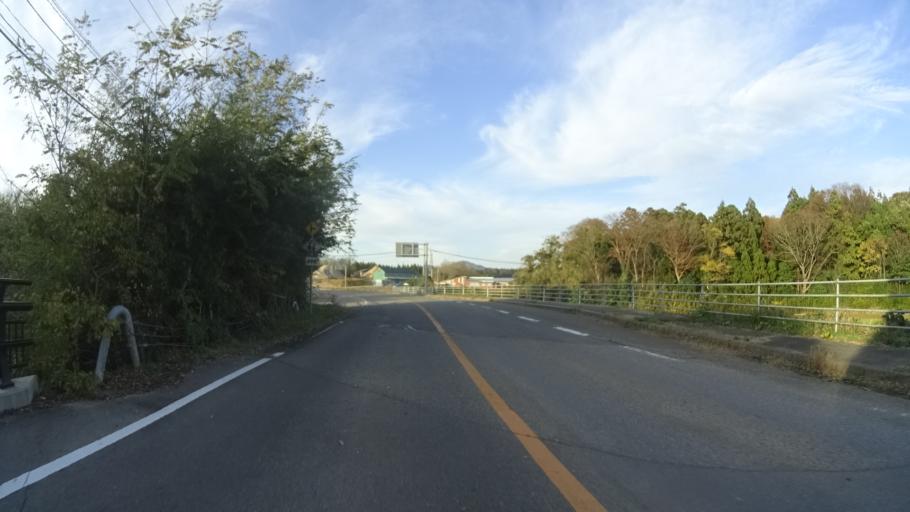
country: JP
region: Ishikawa
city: Nanao
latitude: 37.1549
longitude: 136.7205
